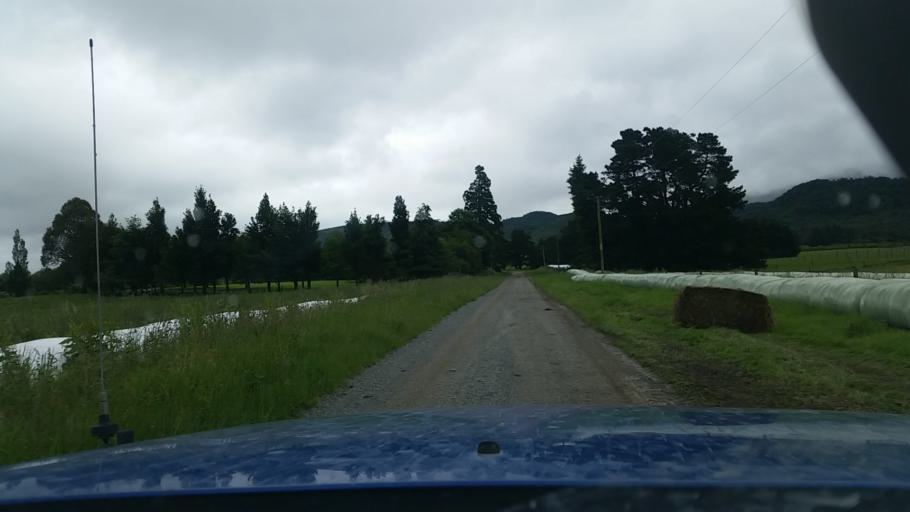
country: NZ
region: Canterbury
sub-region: Ashburton District
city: Methven
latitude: -43.6650
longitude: 171.4172
